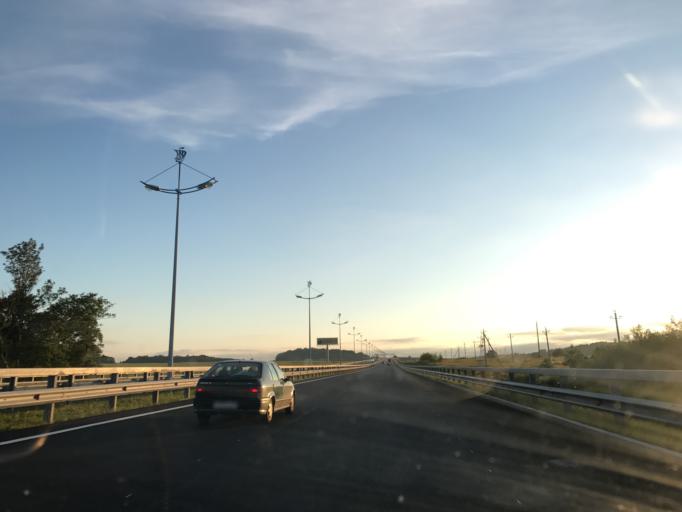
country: RU
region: Kaliningrad
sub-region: Gorod Kaliningrad
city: Pionerskiy
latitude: 54.9209
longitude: 20.2901
